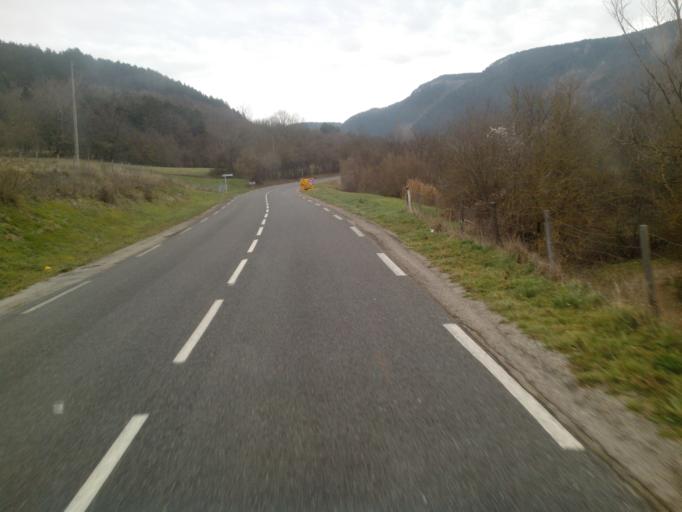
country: FR
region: Languedoc-Roussillon
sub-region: Departement de la Lozere
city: Mende
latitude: 44.4645
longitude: 3.5164
